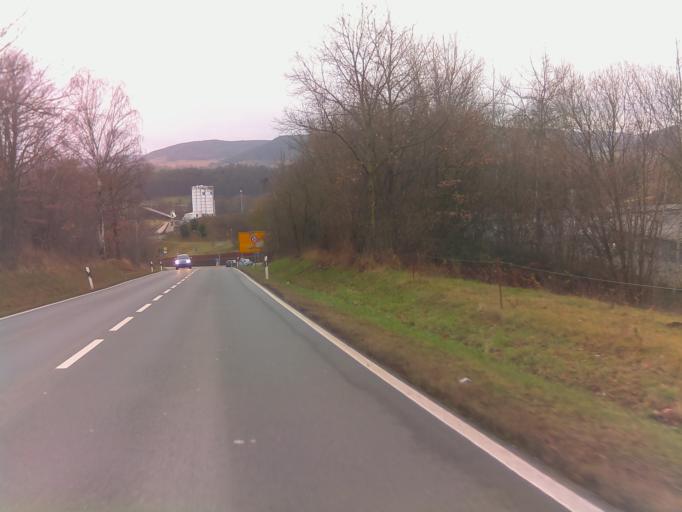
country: DE
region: Thuringia
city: Zollnitz
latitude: 50.8791
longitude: 11.6430
